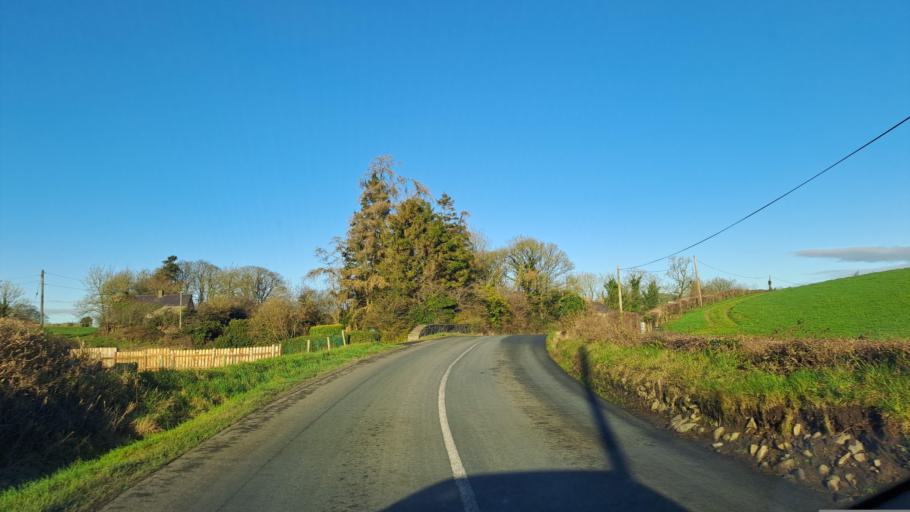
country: IE
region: Ulster
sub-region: An Cabhan
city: Mullagh
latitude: 53.8517
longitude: -6.9610
